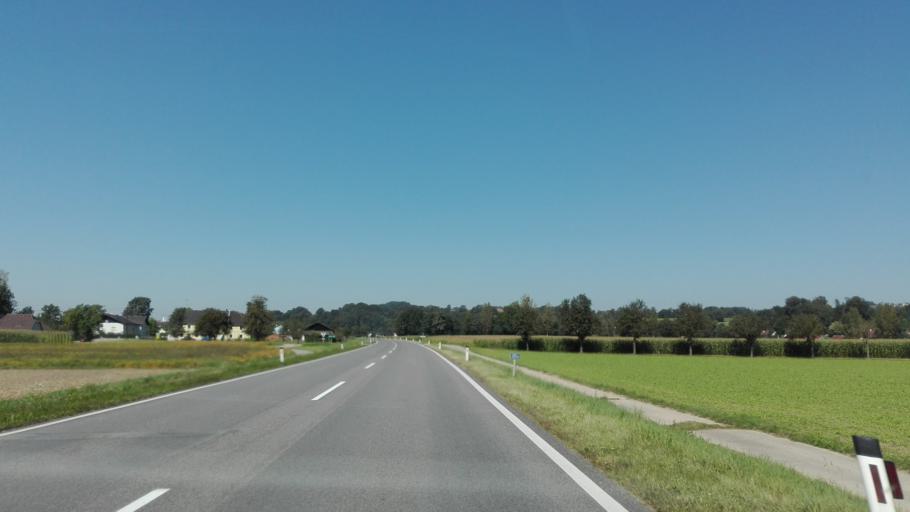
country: AT
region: Upper Austria
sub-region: Politischer Bezirk Perg
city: Bad Kreuzen
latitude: 48.2176
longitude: 14.7388
